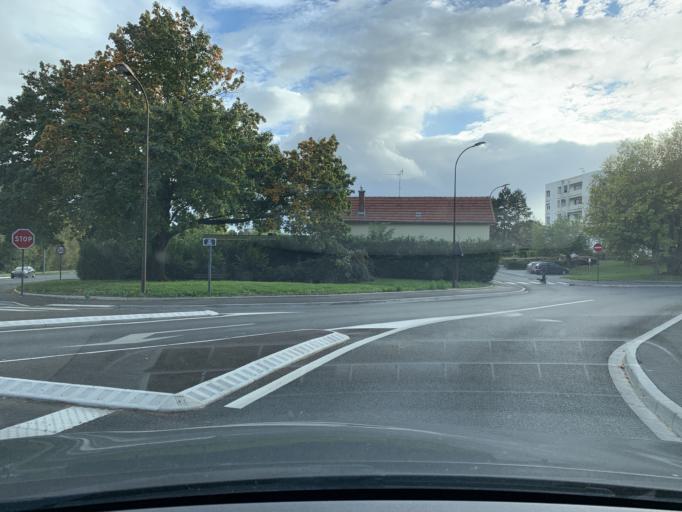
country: FR
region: Picardie
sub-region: Departement de l'Aisne
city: Harly
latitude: 49.8571
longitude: 3.3104
